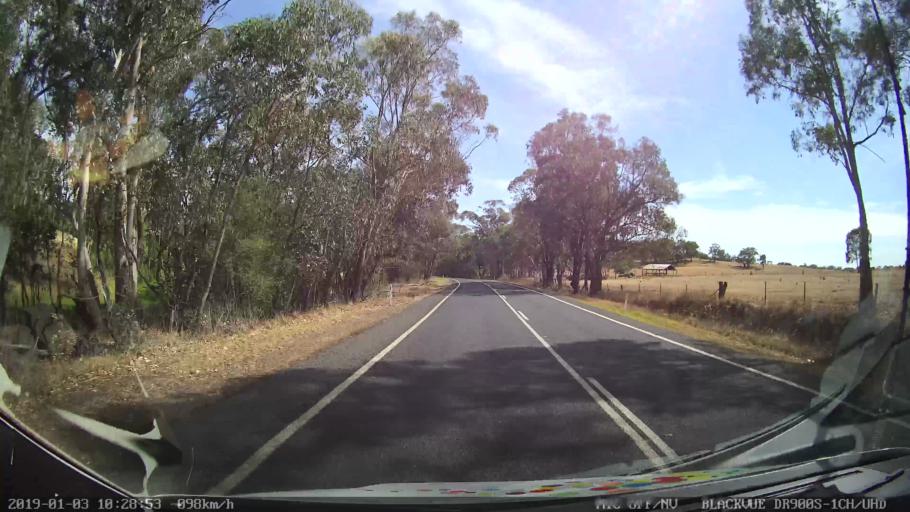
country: AU
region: New South Wales
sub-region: Young
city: Young
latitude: -34.3814
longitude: 148.2600
